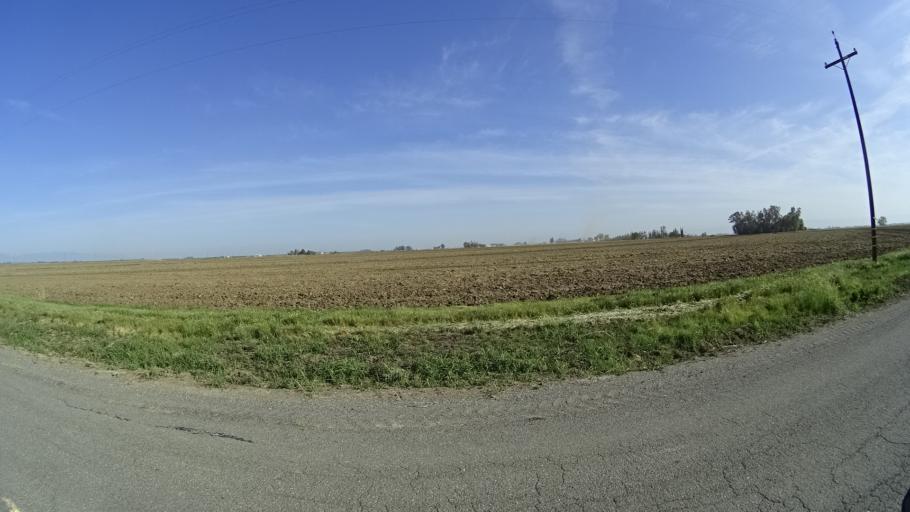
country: US
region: California
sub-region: Glenn County
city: Willows
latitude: 39.5531
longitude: -122.1125
